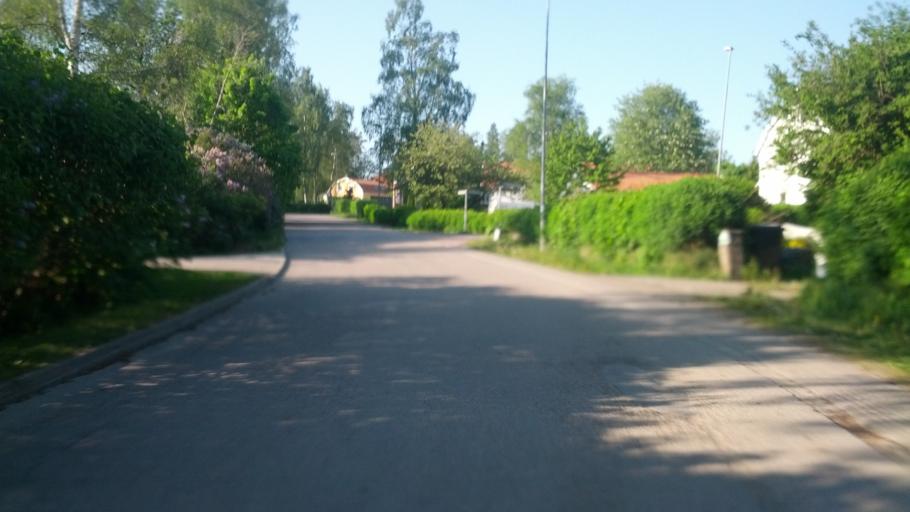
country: SE
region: Stockholm
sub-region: Vallentuna Kommun
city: Vallentuna
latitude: 59.5017
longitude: 18.0783
